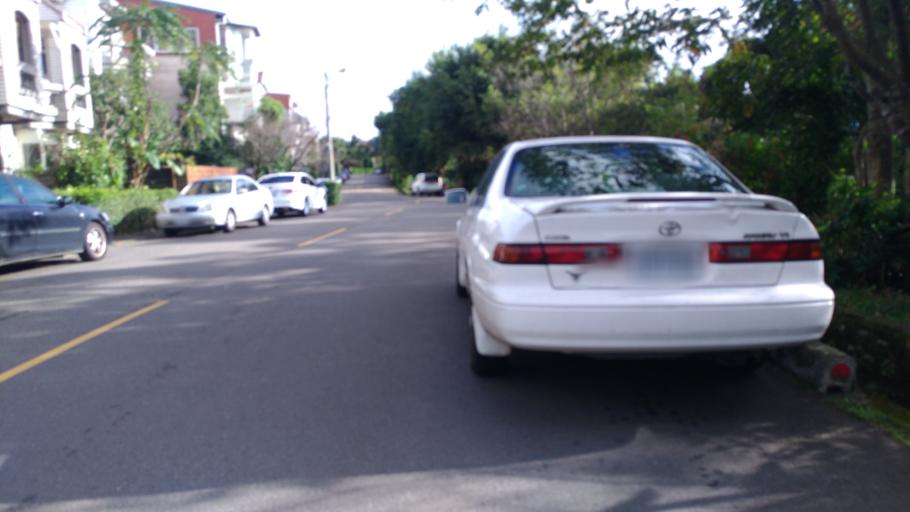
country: TW
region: Taiwan
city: Daxi
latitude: 24.8831
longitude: 121.1722
